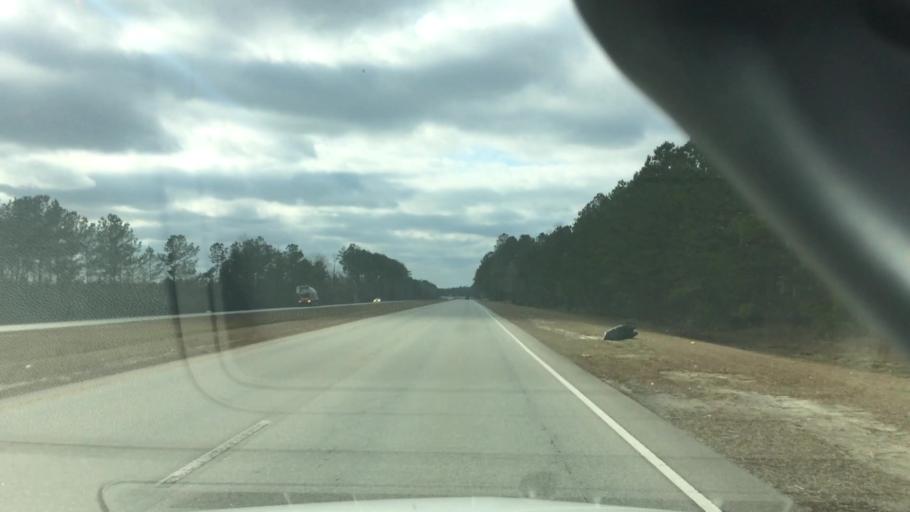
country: US
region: North Carolina
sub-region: Brunswick County
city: Bolivia
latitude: 34.0668
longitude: -78.1833
